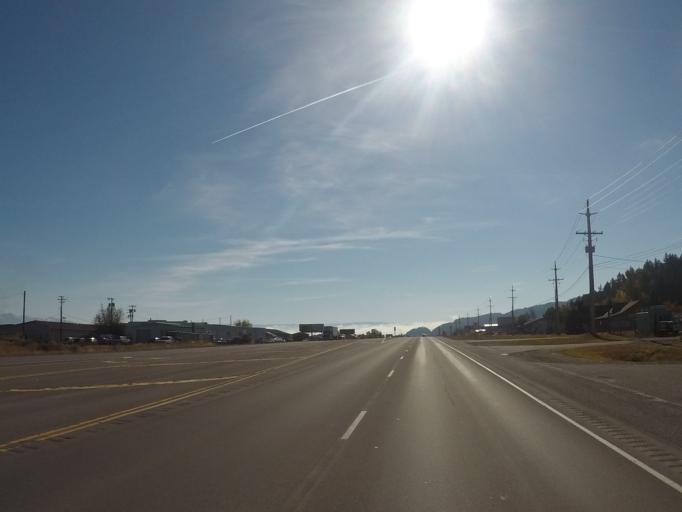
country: US
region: Montana
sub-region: Flathead County
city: Somers
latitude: 48.1244
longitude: -114.2615
